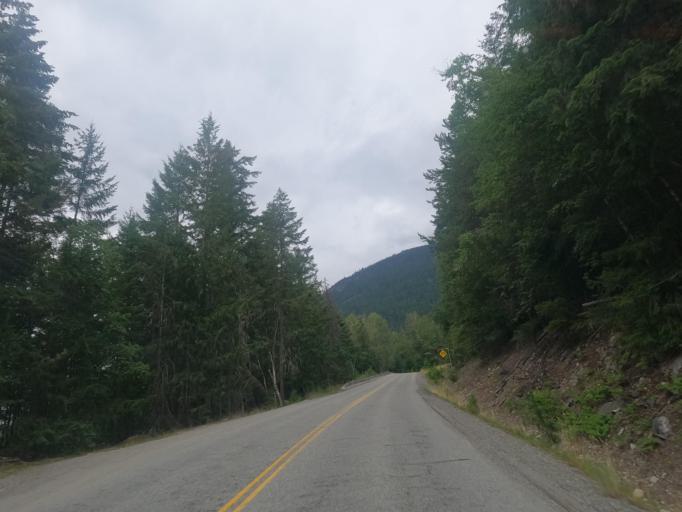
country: CA
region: British Columbia
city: Pemberton
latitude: 50.3021
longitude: -122.5849
